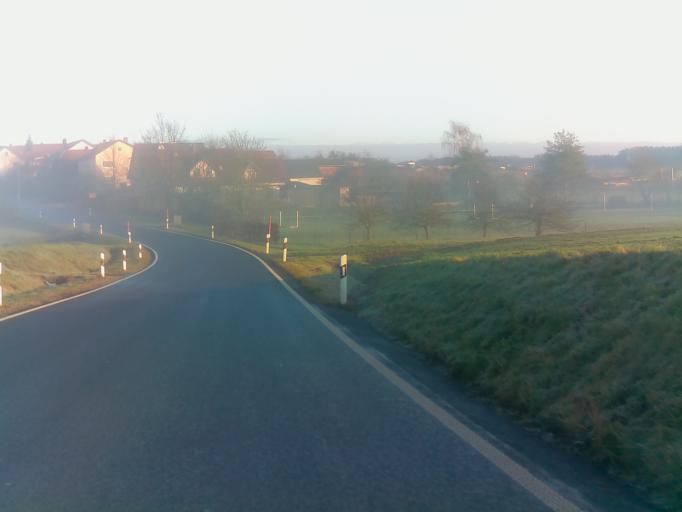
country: DE
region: Bavaria
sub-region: Regierungsbezirk Unterfranken
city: Neunkirchen
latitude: 49.7019
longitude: 9.4014
